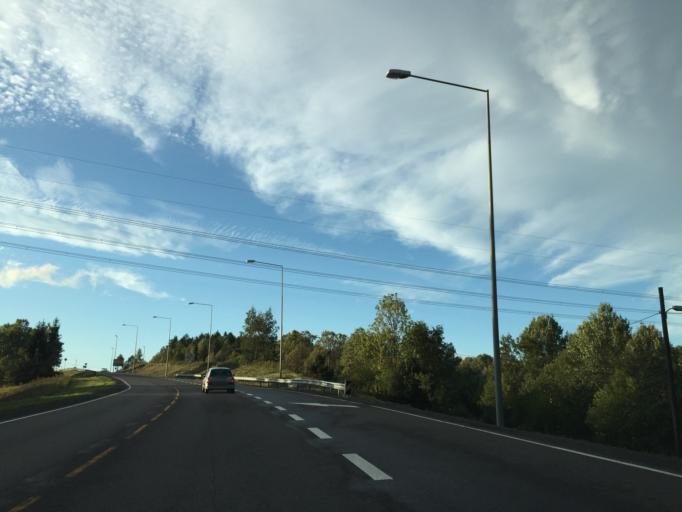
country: NO
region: Akershus
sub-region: Oppegard
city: Kolbotn
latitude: 59.8371
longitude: 10.8423
